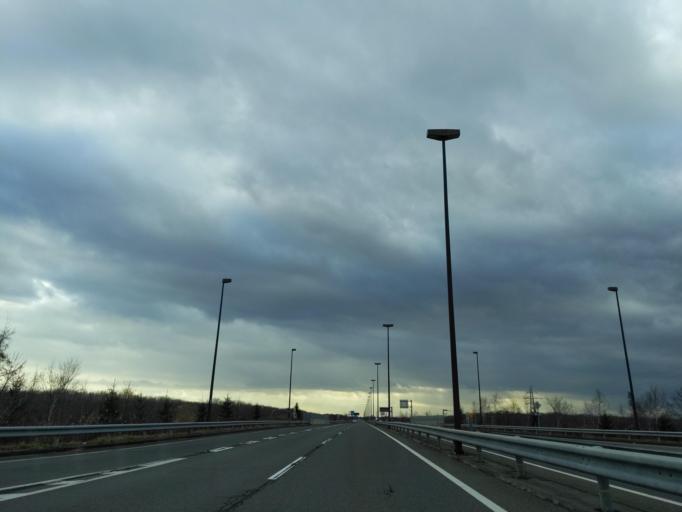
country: JP
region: Hokkaido
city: Chitose
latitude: 42.8264
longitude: 141.6884
